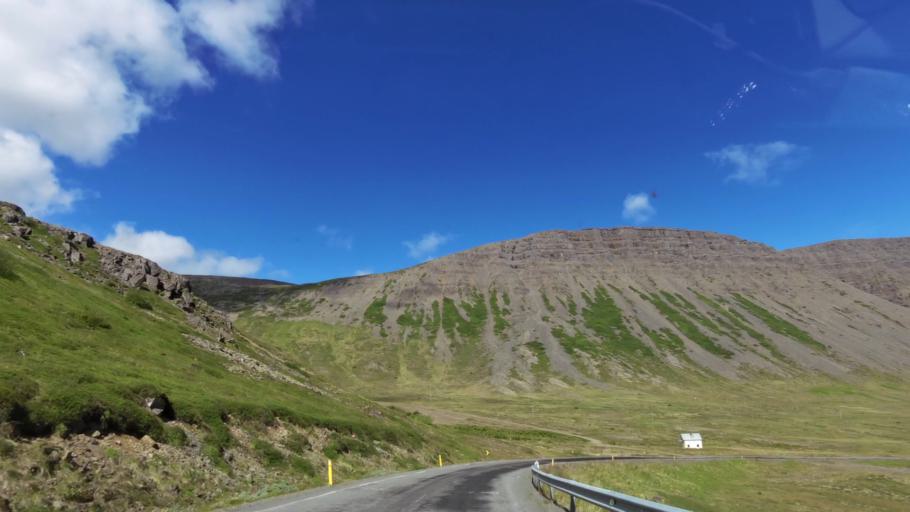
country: IS
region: Westfjords
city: Isafjoerdur
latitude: 65.6635
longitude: -23.6397
